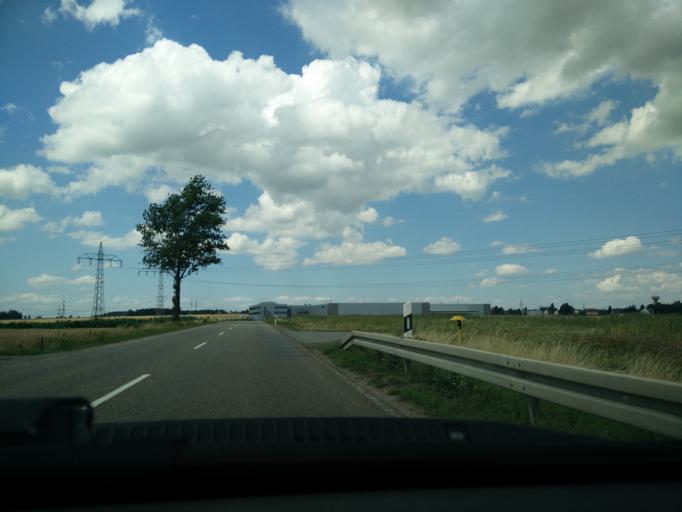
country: DE
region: Saxony
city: Wittgensdorf
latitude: 50.8690
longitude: 12.8427
